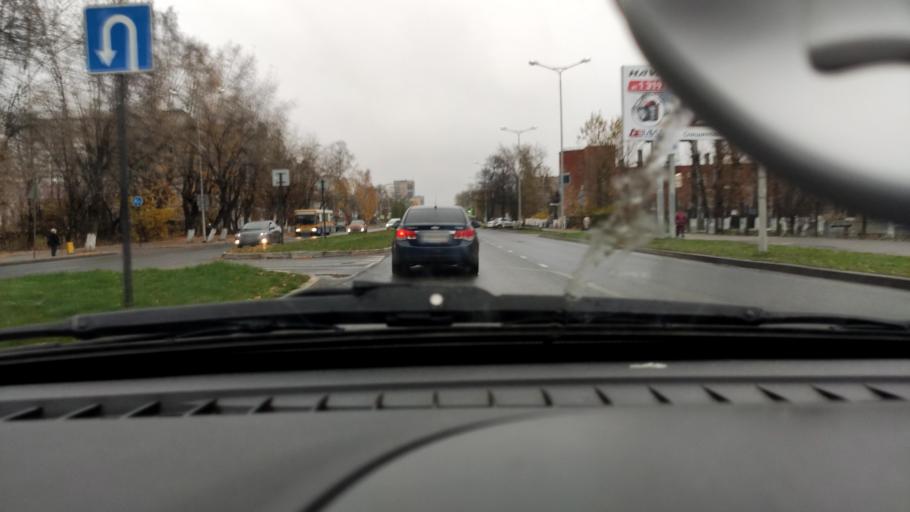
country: RU
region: Perm
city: Kultayevo
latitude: 58.0002
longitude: 55.9432
